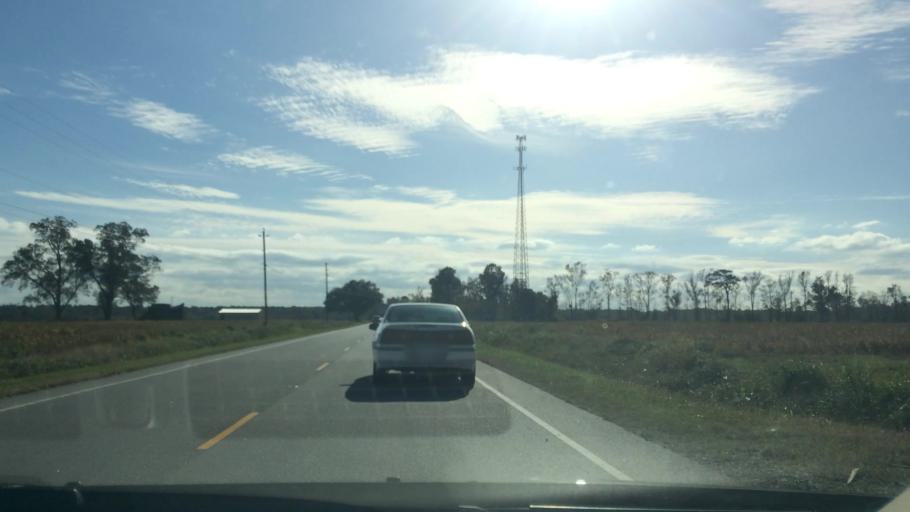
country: US
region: North Carolina
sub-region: Greene County
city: Snow Hill
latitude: 35.4717
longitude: -77.6594
